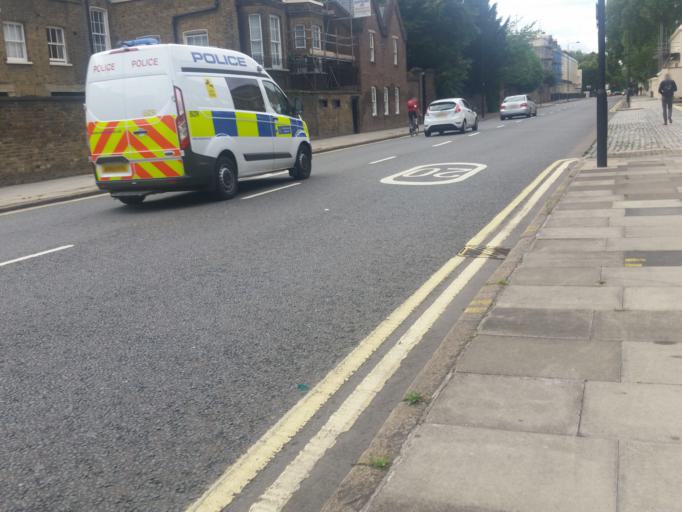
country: GB
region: England
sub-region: Greater London
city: Camden Town
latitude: 51.5331
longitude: -0.1459
